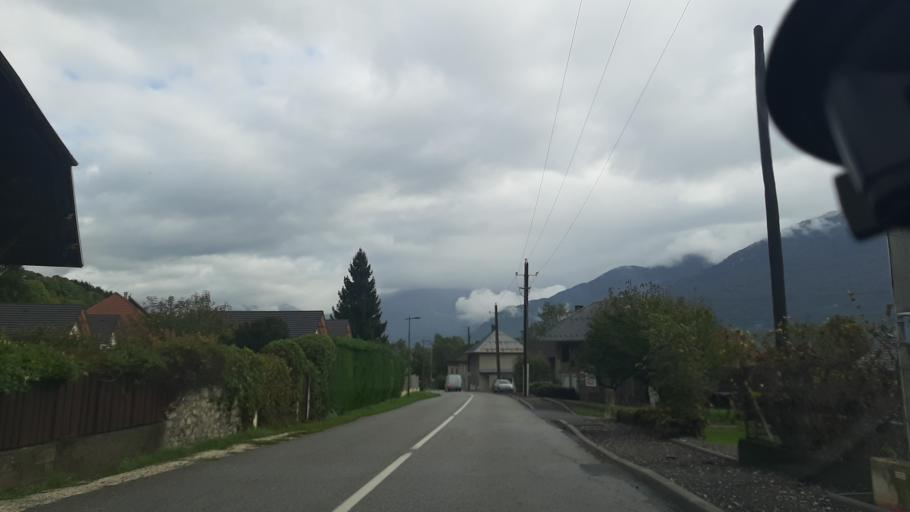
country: FR
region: Rhone-Alpes
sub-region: Departement de la Savoie
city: Frontenex
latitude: 45.6273
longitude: 6.3009
